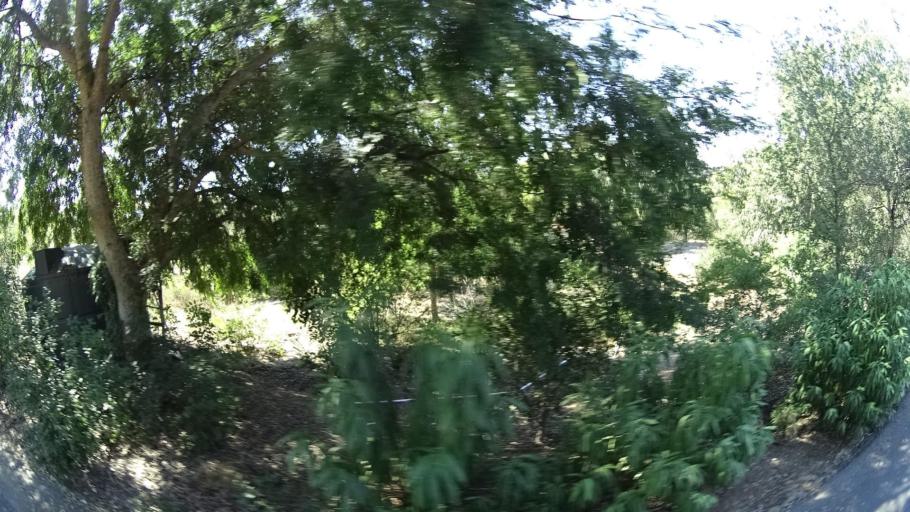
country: US
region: California
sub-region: San Diego County
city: Crest
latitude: 32.8224
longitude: -116.8541
